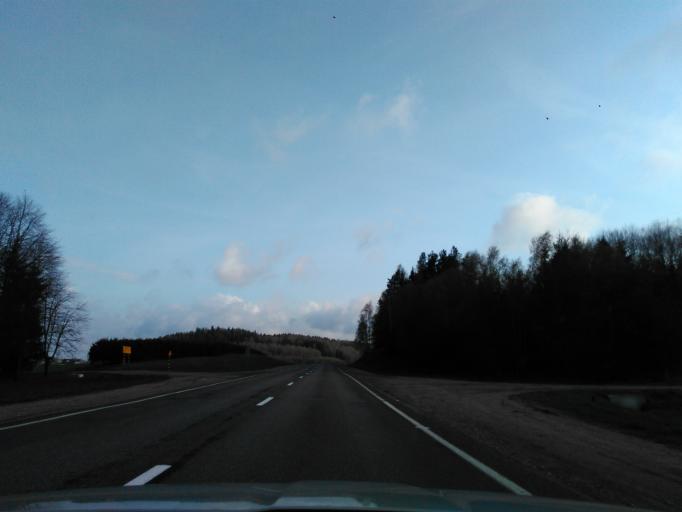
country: BY
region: Minsk
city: Lahoysk
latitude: 54.2247
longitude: 27.8335
